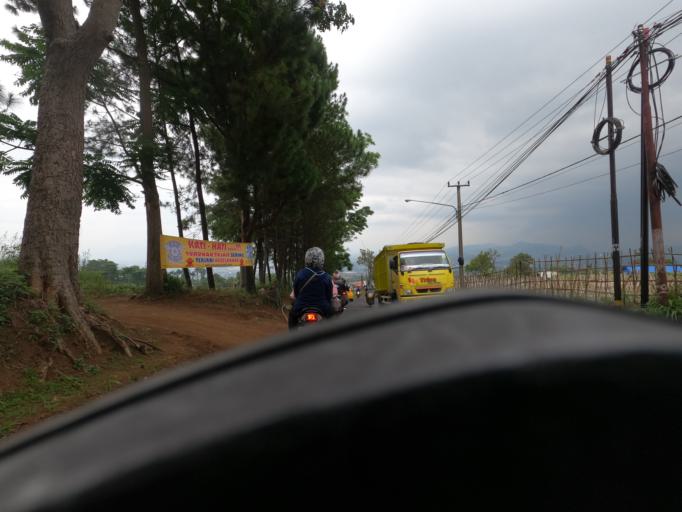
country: ID
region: West Java
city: Cimahi
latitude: -6.8301
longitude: 107.5215
